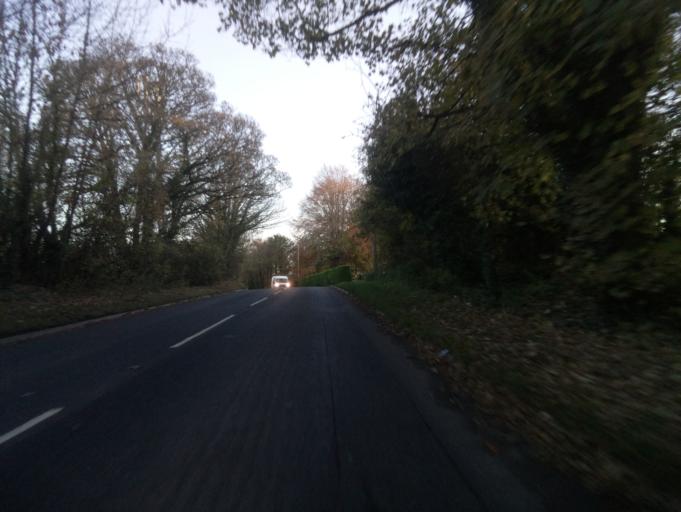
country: GB
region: England
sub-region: Wiltshire
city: Upton Scudamore
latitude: 51.2155
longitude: -2.1986
